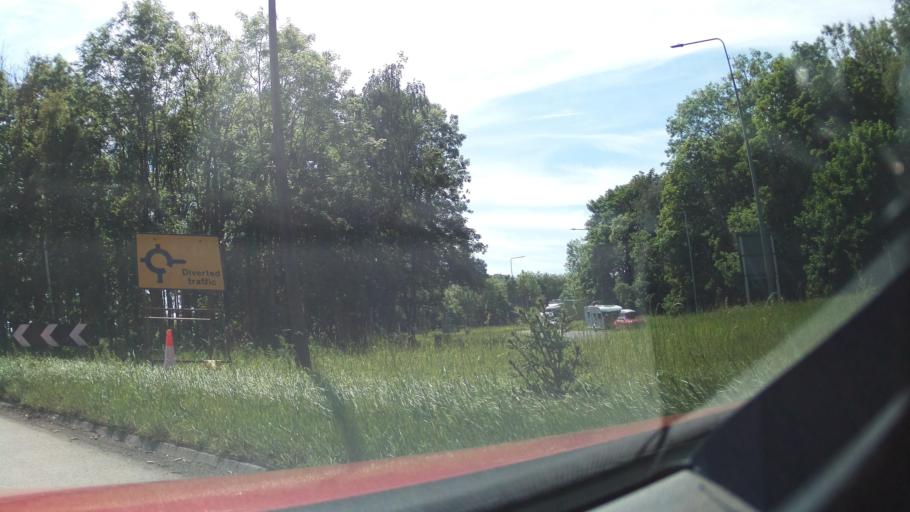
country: GB
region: England
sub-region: North Lincolnshire
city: Broughton
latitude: 53.5488
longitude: -0.5583
